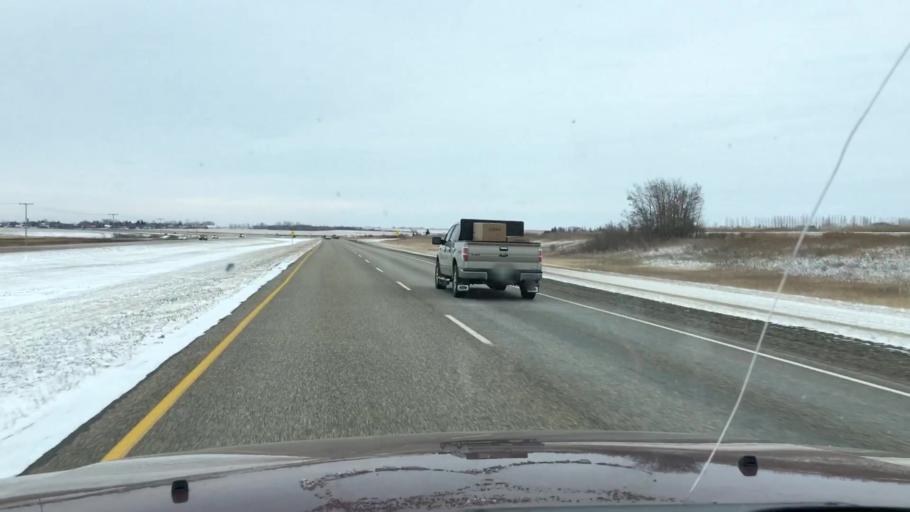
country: CA
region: Saskatchewan
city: Moose Jaw
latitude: 50.9537
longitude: -105.7096
